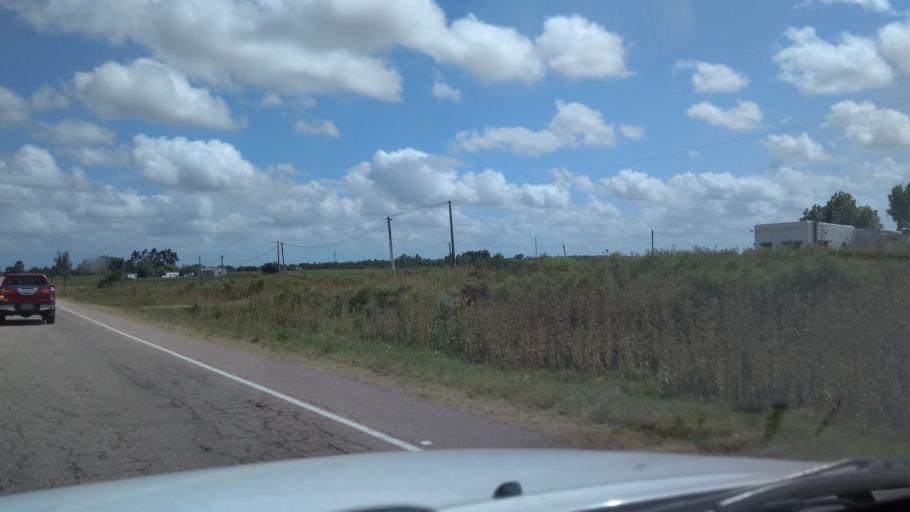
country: UY
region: Canelones
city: Sauce
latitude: -34.6328
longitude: -56.0519
